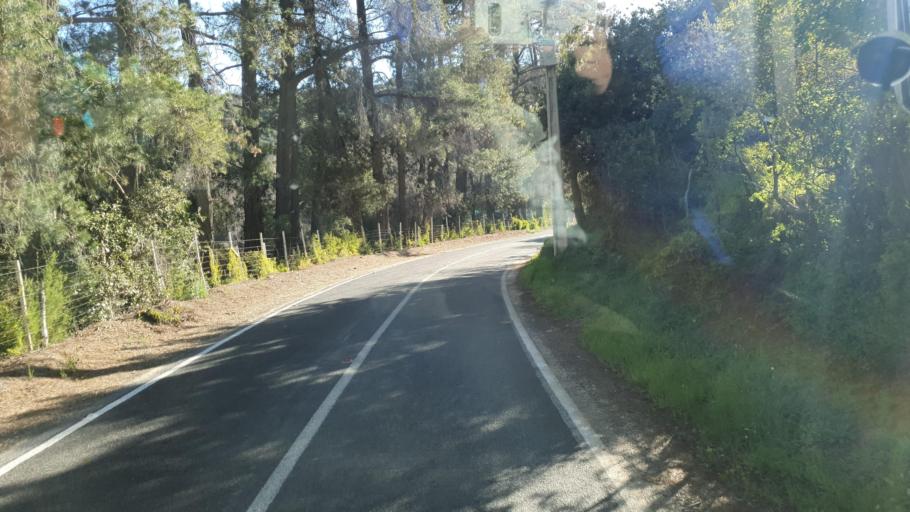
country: CL
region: Valparaiso
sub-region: Provincia de Marga Marga
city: Limache
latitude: -33.1786
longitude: -71.1720
